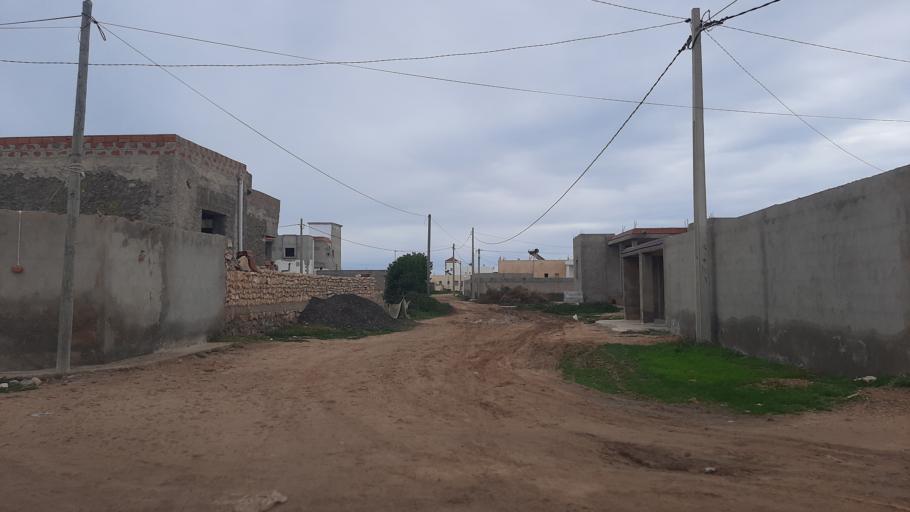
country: TN
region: Safaqis
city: Al Qarmadah
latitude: 34.7995
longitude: 10.8533
